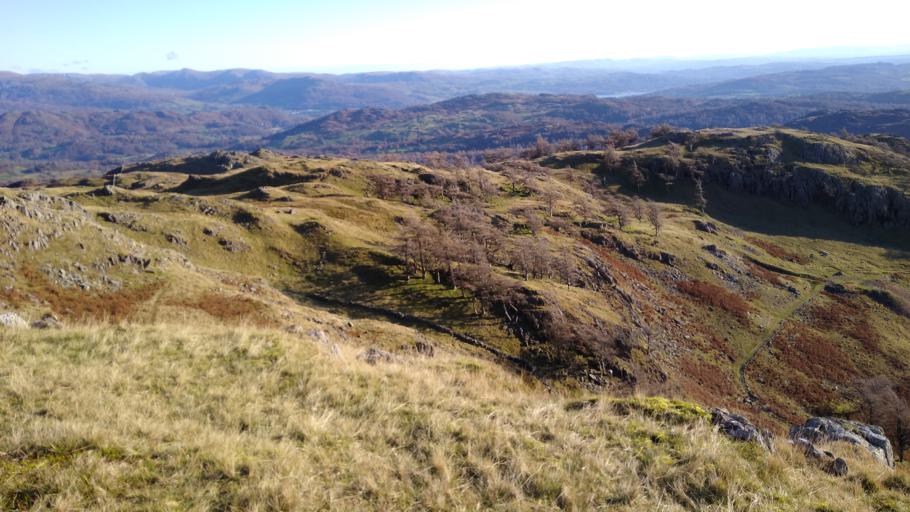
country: GB
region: England
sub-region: Cumbria
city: Ambleside
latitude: 54.4050
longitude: -3.0853
